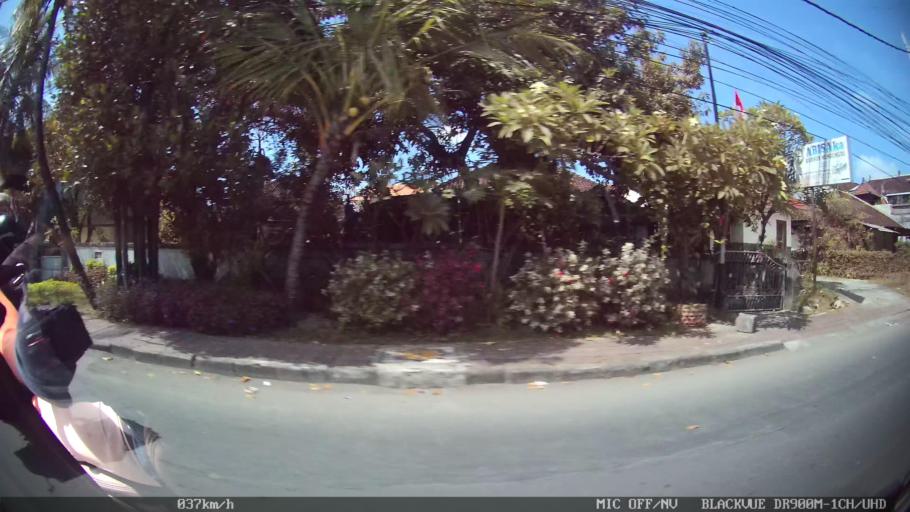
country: ID
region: Bali
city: Kuta
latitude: -8.6724
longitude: 115.1701
